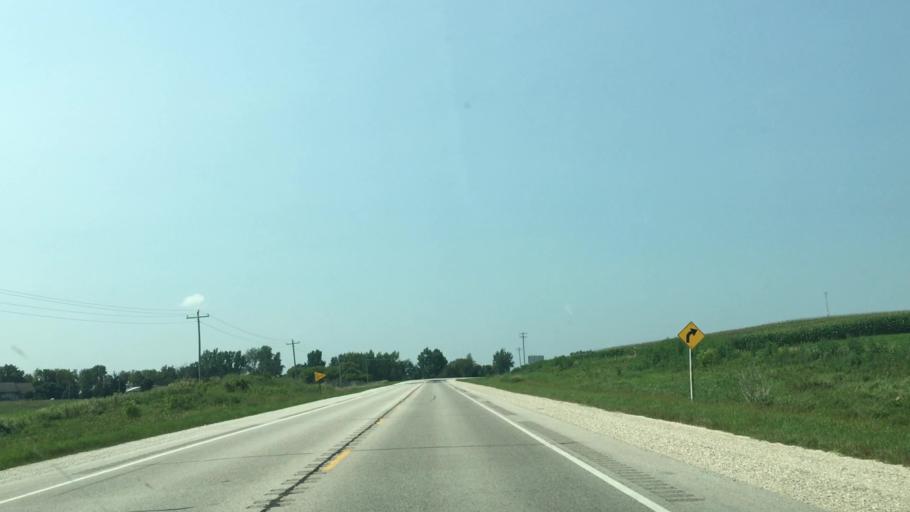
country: US
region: Iowa
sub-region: Winneshiek County
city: Decorah
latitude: 43.1924
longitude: -91.8694
